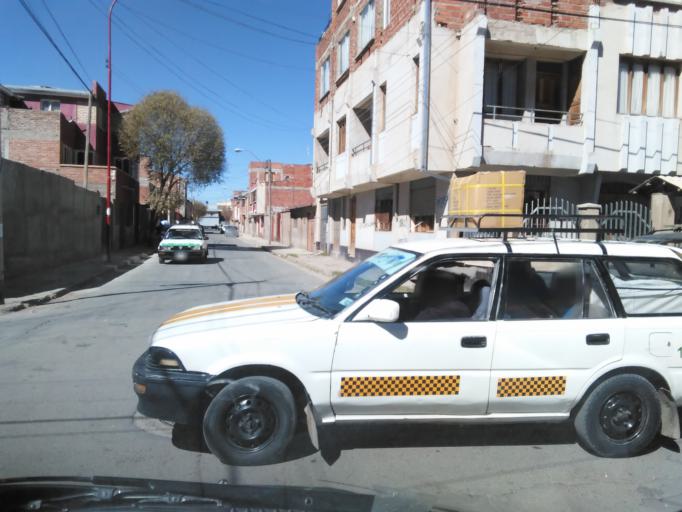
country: BO
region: Oruro
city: Oruro
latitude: -17.9622
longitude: -67.1028
